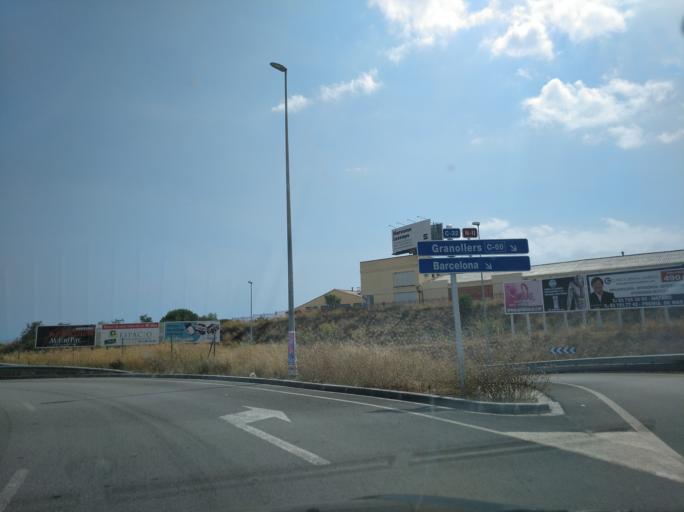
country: ES
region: Catalonia
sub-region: Provincia de Barcelona
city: Mataro
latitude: 41.5534
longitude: 2.4307
